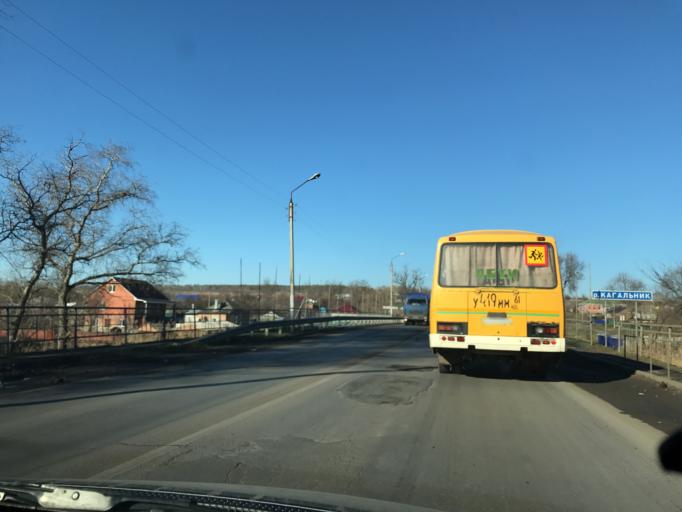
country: RU
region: Rostov
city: Kagal'nitskaya
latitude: 46.8848
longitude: 40.1450
